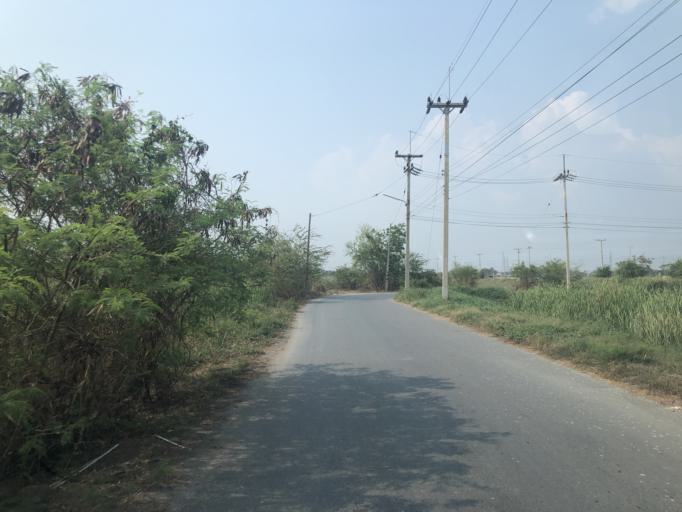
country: TH
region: Chachoengsao
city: Bang Pakong
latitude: 13.5120
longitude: 100.9410
